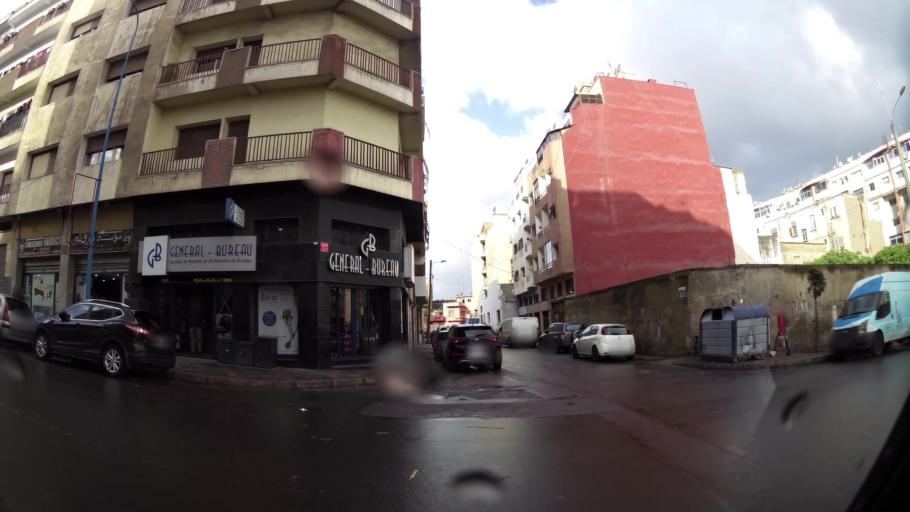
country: MA
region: Grand Casablanca
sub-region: Casablanca
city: Casablanca
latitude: 33.5847
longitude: -7.6000
